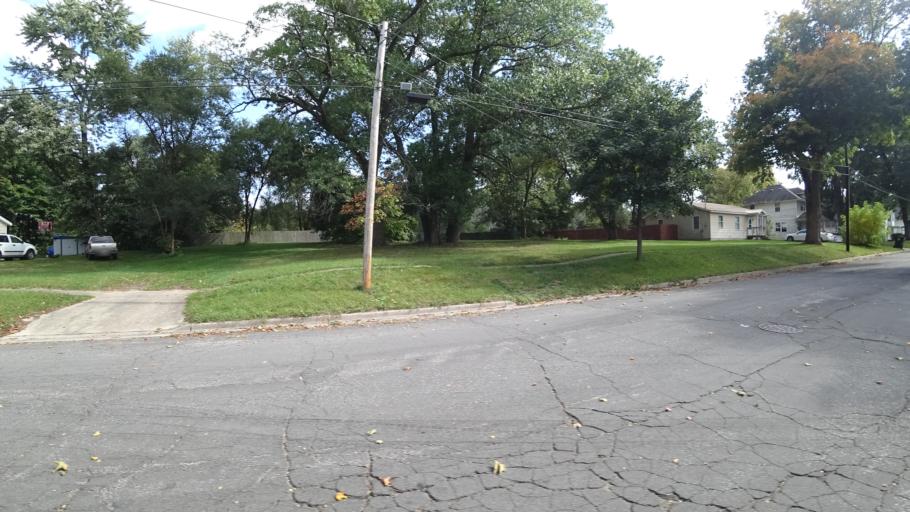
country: US
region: Michigan
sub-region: Saint Joseph County
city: Three Rivers
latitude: 41.9372
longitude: -85.6236
